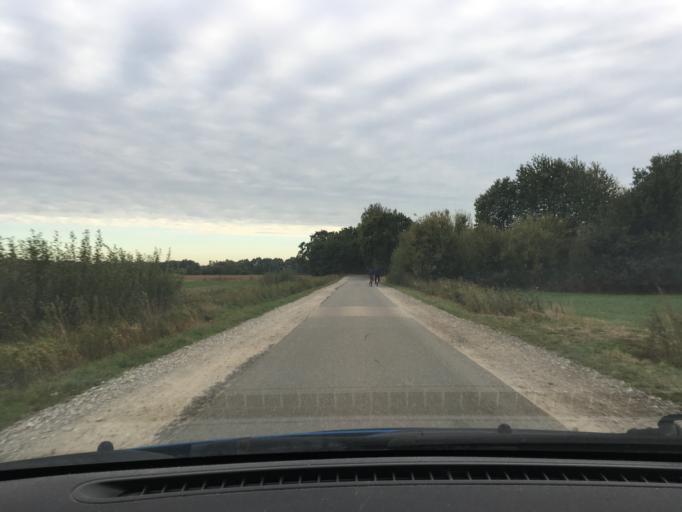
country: DE
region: Lower Saxony
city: Winsen
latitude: 53.3695
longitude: 10.2377
